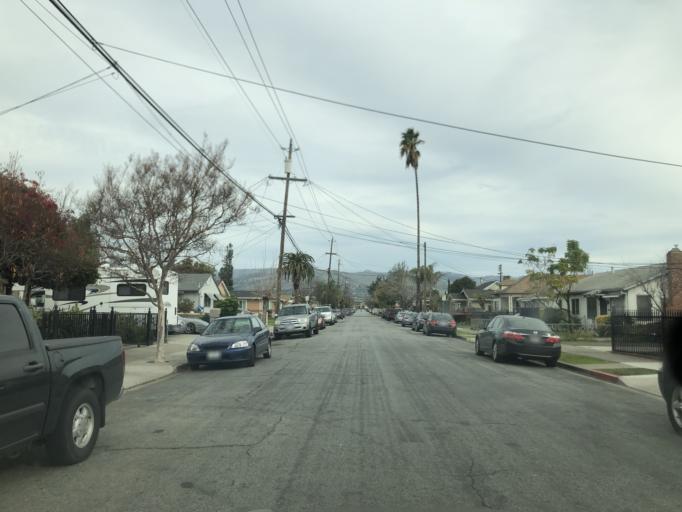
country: US
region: California
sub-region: Santa Clara County
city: Alum Rock
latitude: 37.3482
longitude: -121.8584
